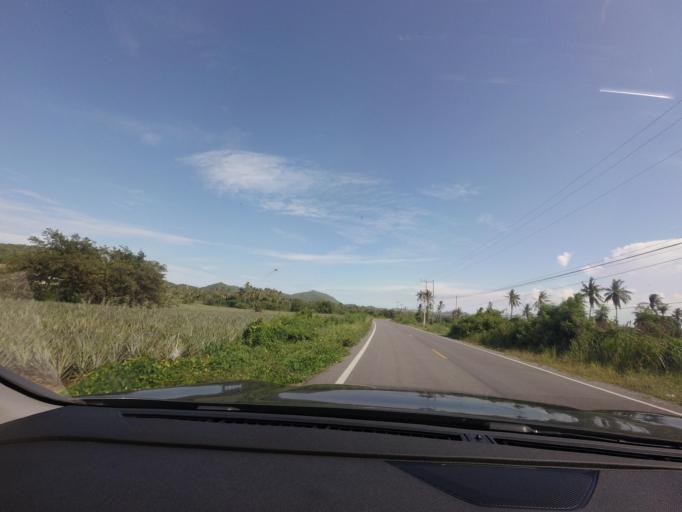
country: TH
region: Prachuap Khiri Khan
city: Pran Buri
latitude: 12.4511
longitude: 99.9444
